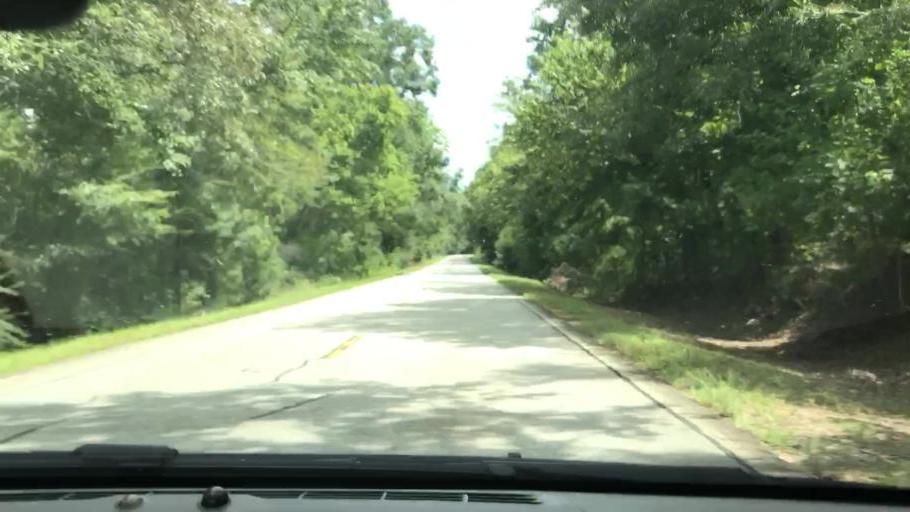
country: US
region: Georgia
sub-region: Quitman County
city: Georgetown
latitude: 32.0416
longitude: -85.0321
